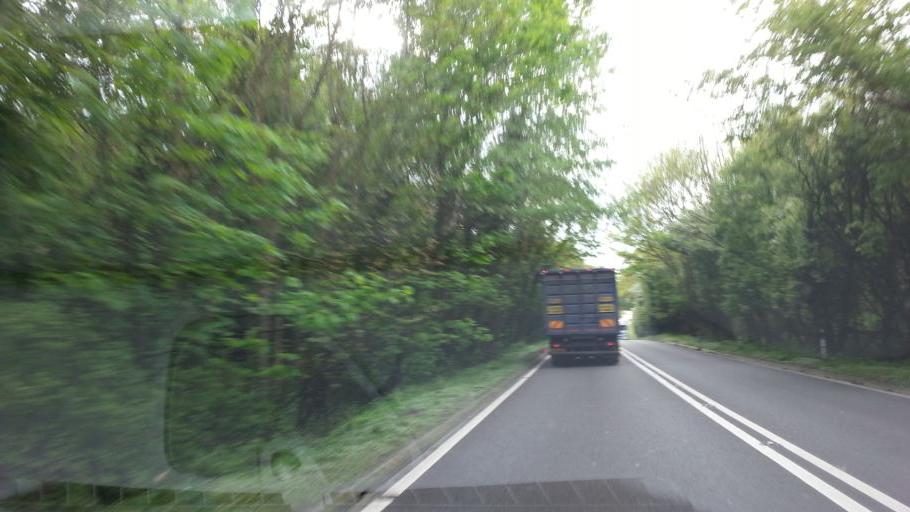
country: GB
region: England
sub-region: Nottinghamshire
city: South Collingham
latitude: 53.0798
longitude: -0.7126
